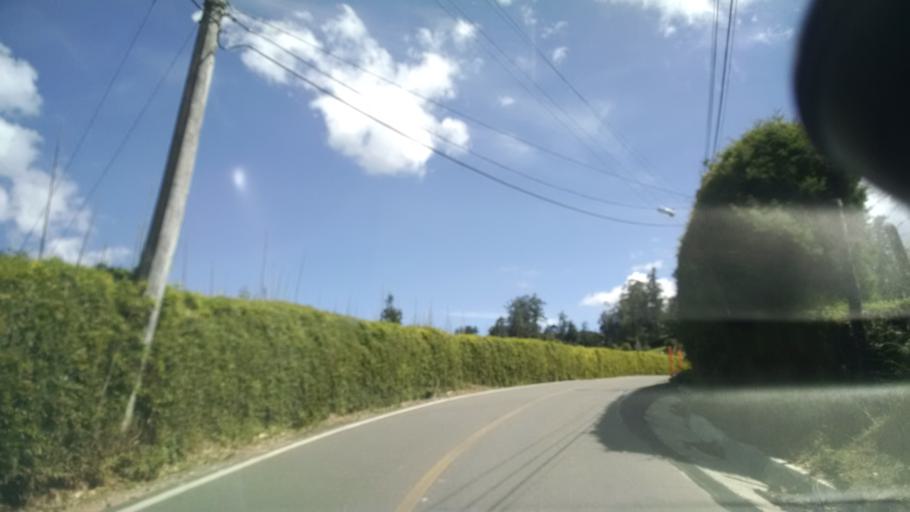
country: CO
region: Antioquia
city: El Retiro
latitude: 6.0874
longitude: -75.5022
